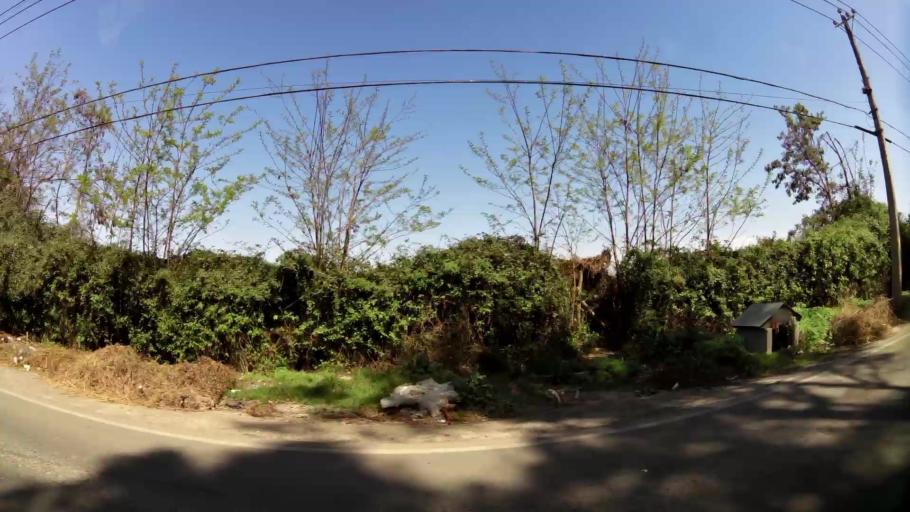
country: CL
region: Santiago Metropolitan
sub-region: Provincia de Santiago
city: Lo Prado
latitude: -33.3912
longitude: -70.7778
